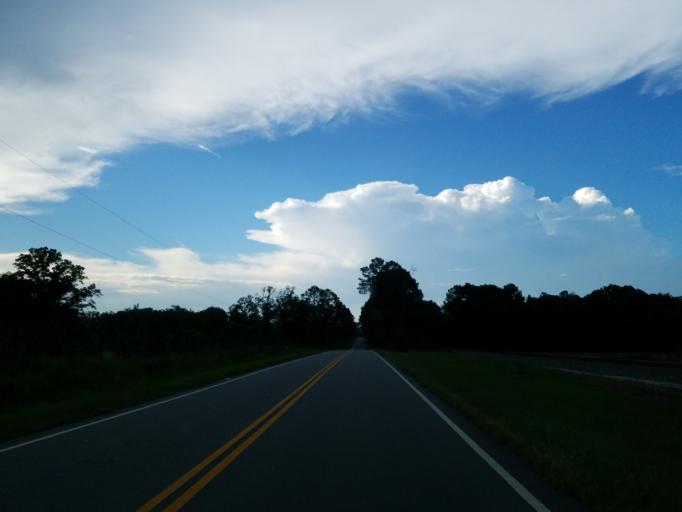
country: US
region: Georgia
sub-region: Tift County
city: Unionville
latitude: 31.3444
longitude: -83.4829
